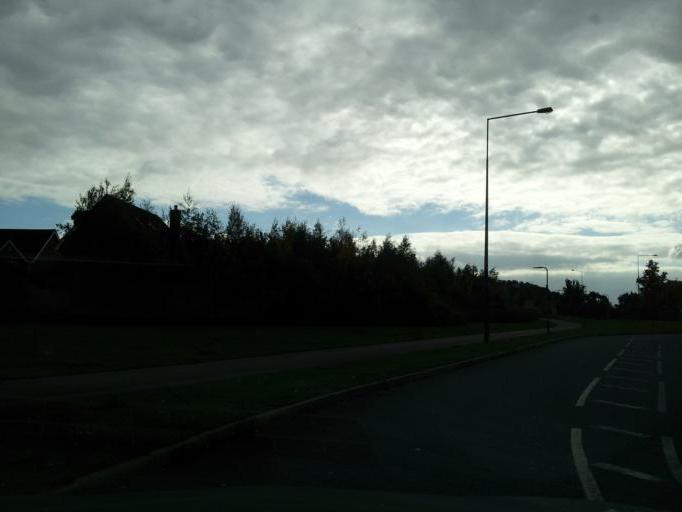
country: GB
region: England
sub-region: Milton Keynes
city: Shenley Church End
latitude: 52.0026
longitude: -0.8067
